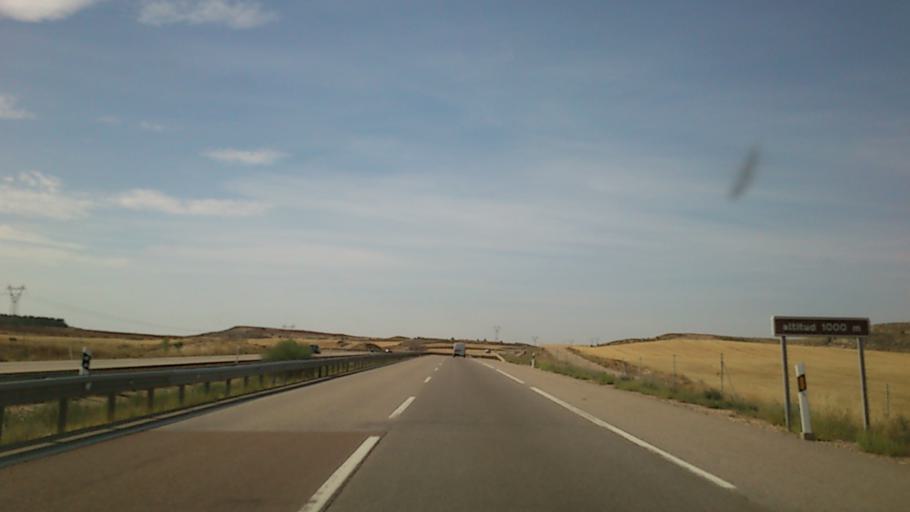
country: ES
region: Aragon
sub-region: Provincia de Teruel
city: Ferreruela de Huerva
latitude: 40.9995
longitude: -1.2637
